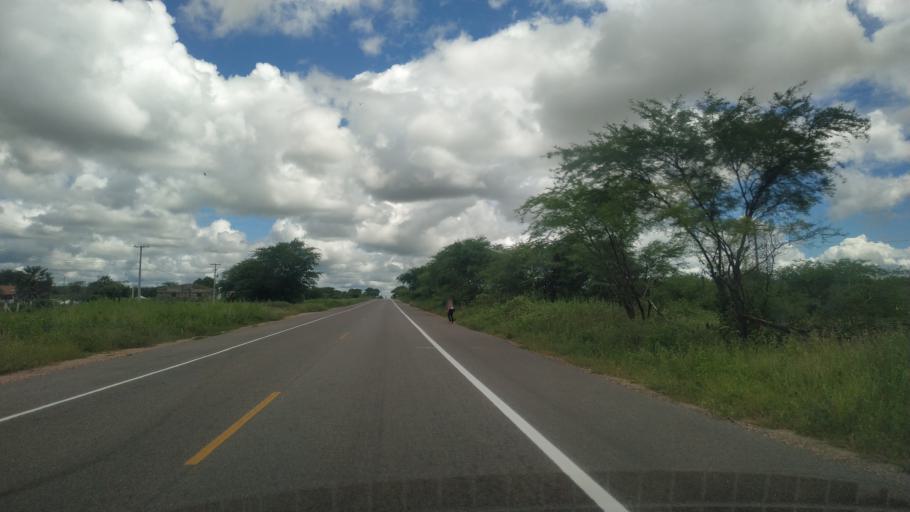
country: BR
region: Rio Grande do Norte
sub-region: Areia Branca
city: Areia Branca
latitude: -5.0566
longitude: -37.1549
